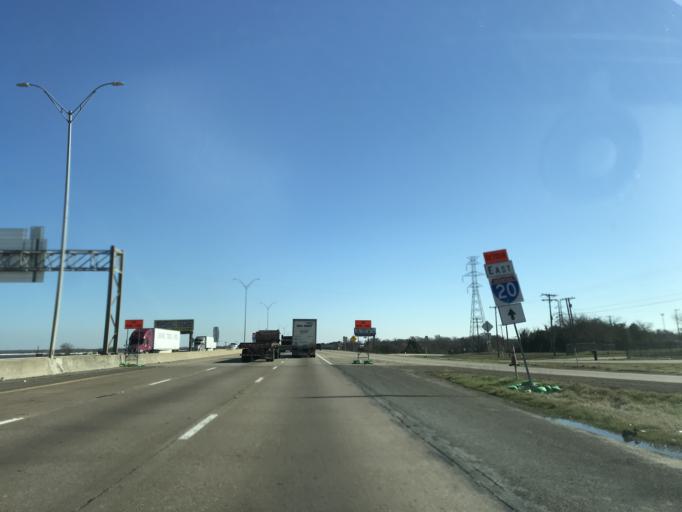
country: US
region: Texas
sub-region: Dallas County
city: Hutchins
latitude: 32.6565
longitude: -96.7185
